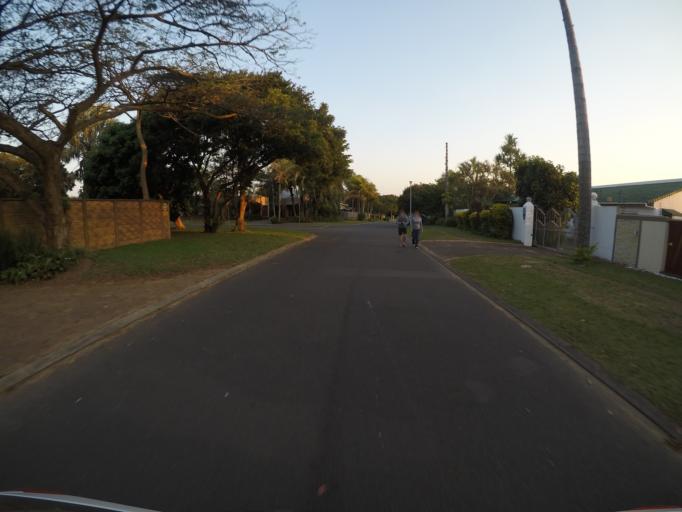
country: ZA
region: KwaZulu-Natal
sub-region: uThungulu District Municipality
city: Richards Bay
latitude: -28.7660
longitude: 32.1203
